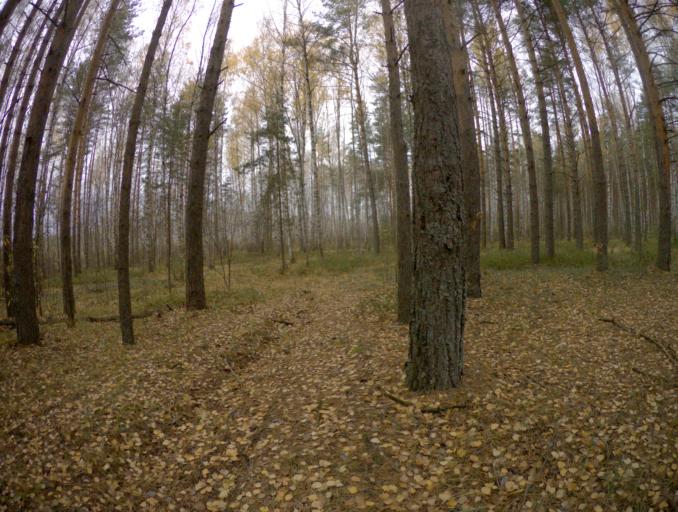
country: RU
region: Vladimir
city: Kommunar
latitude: 56.1040
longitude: 40.4596
